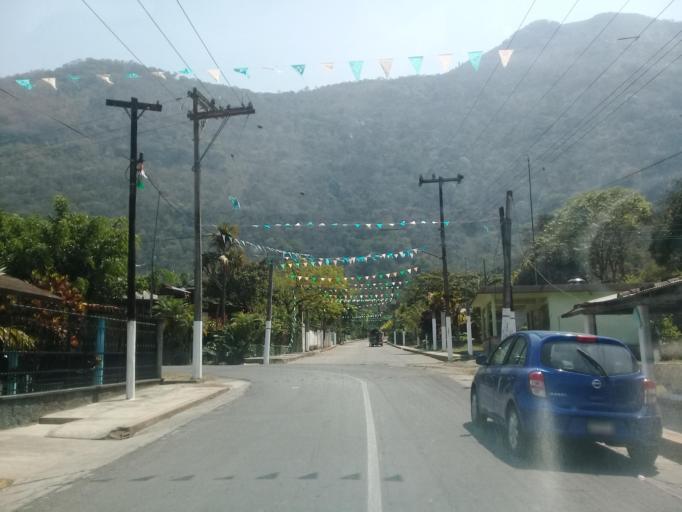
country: MX
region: Veracruz
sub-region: Ixtaczoquitlan
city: Capoluca
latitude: 18.8047
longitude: -96.9872
